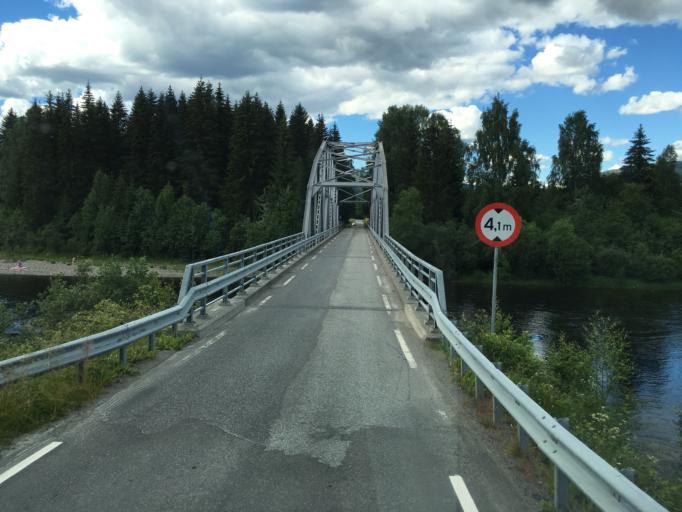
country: NO
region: Oppland
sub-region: Nordre Land
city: Dokka
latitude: 60.8232
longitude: 10.0735
